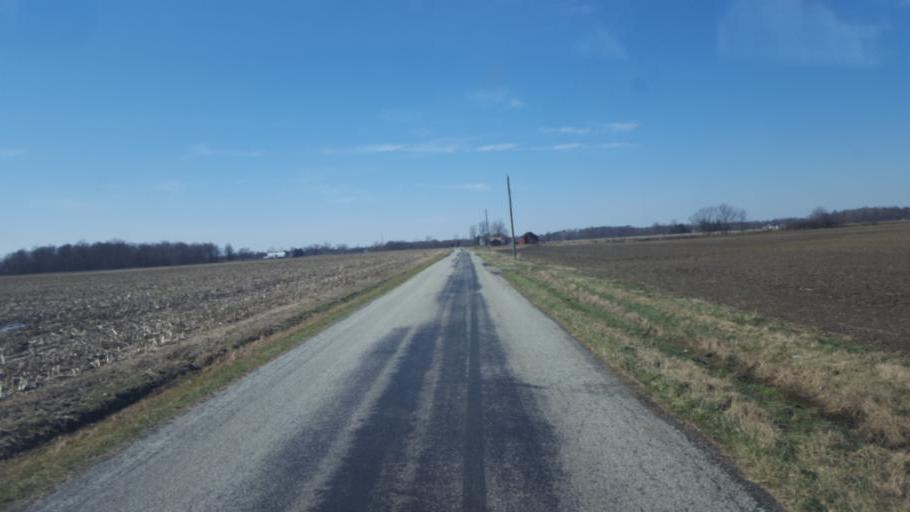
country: US
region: Ohio
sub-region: Marion County
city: Prospect
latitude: 40.4912
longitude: -83.1538
